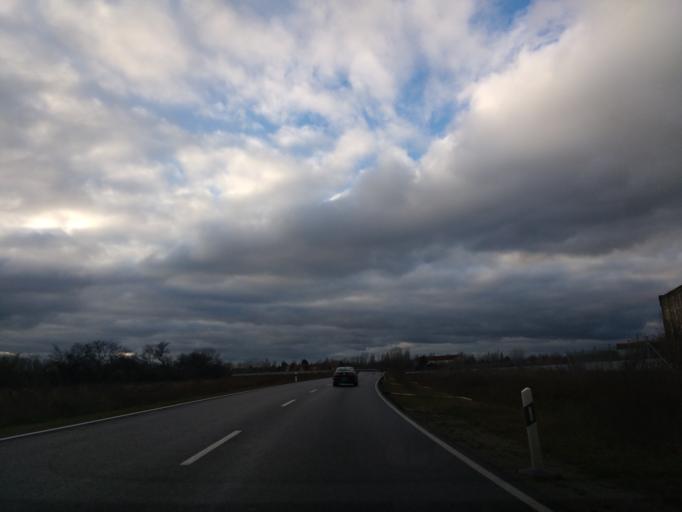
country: DE
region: Saxony-Anhalt
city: Zscherben
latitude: 51.3291
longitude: 11.9874
